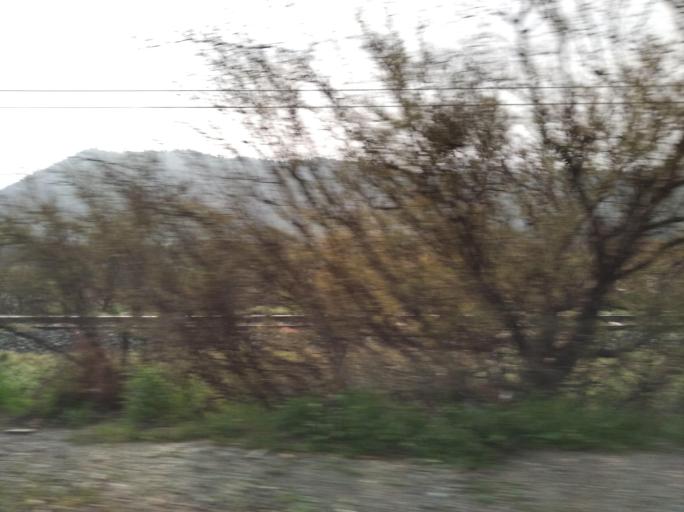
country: CL
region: Santiago Metropolitan
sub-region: Provincia de Chacabuco
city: Lampa
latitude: -33.1409
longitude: -70.9164
